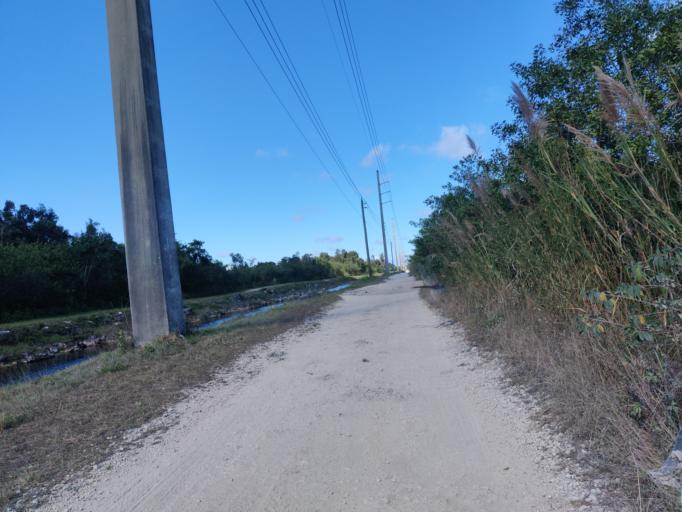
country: US
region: Florida
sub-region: Miami-Dade County
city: Kendall West
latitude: 25.7275
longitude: -80.4651
